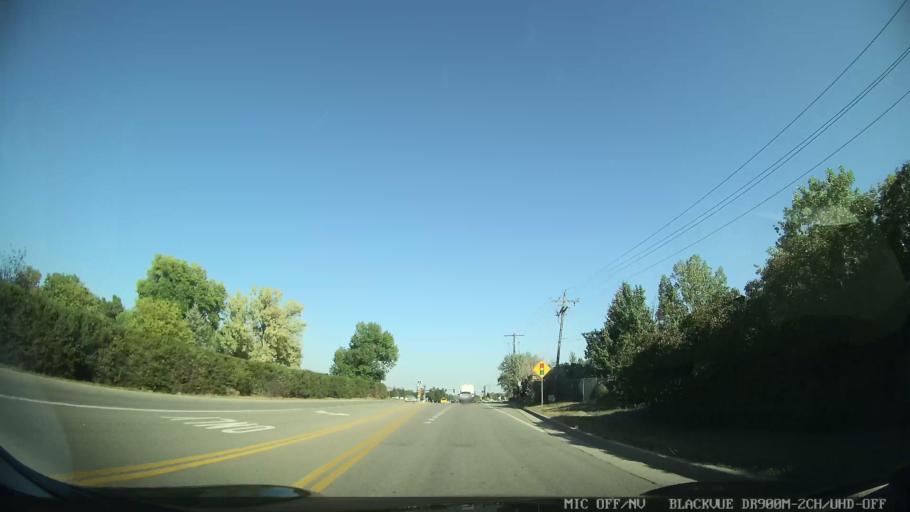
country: US
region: Colorado
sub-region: Larimer County
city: Loveland
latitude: 40.4510
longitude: -105.0805
